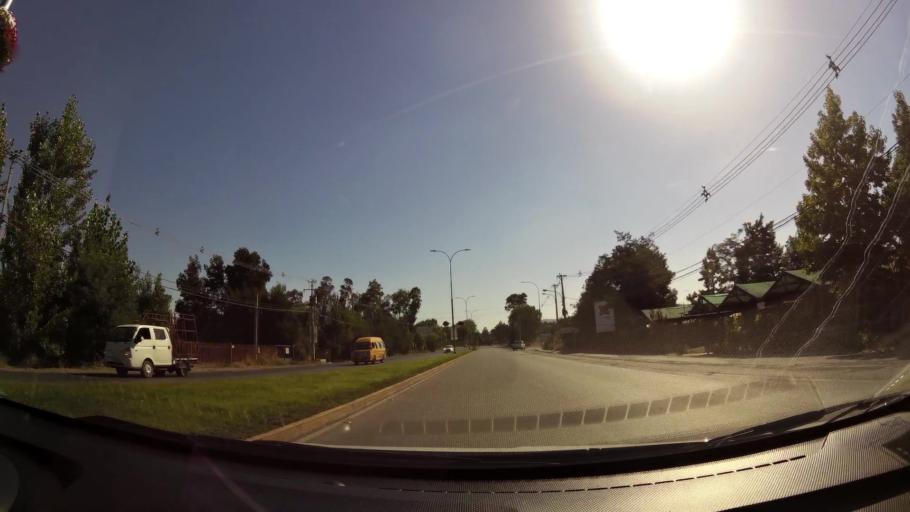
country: CL
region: Maule
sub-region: Provincia de Talca
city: Talca
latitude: -35.4001
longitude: -71.6298
